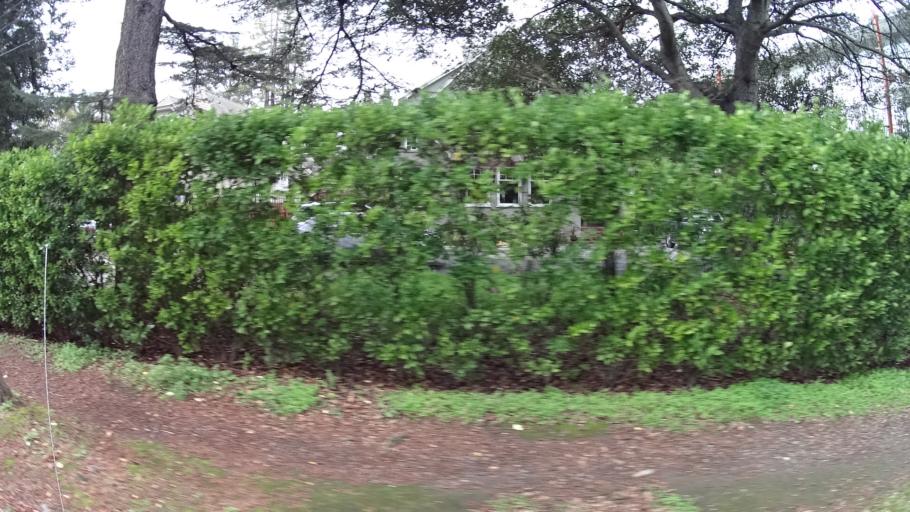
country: US
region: California
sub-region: San Mateo County
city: San Mateo
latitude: 37.5721
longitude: -122.3395
